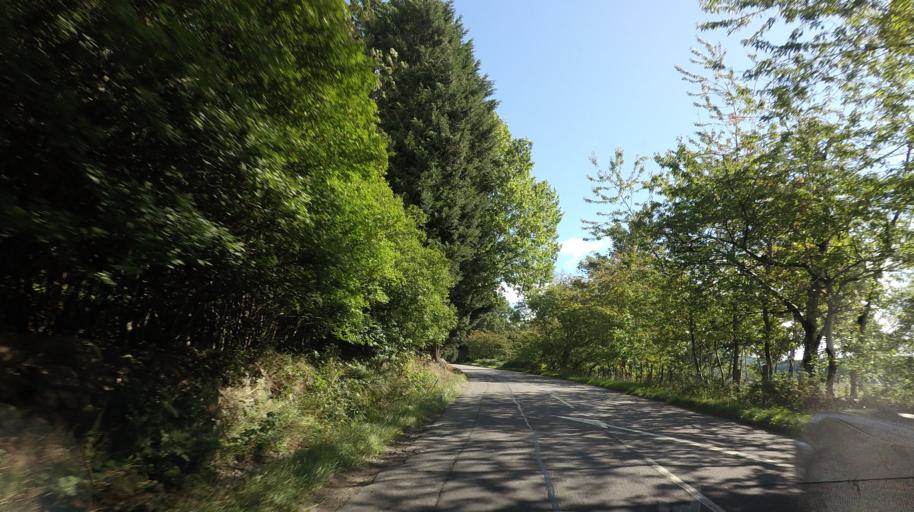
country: GB
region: Scotland
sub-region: Aberdeenshire
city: Banchory
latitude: 57.0570
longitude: -2.4481
